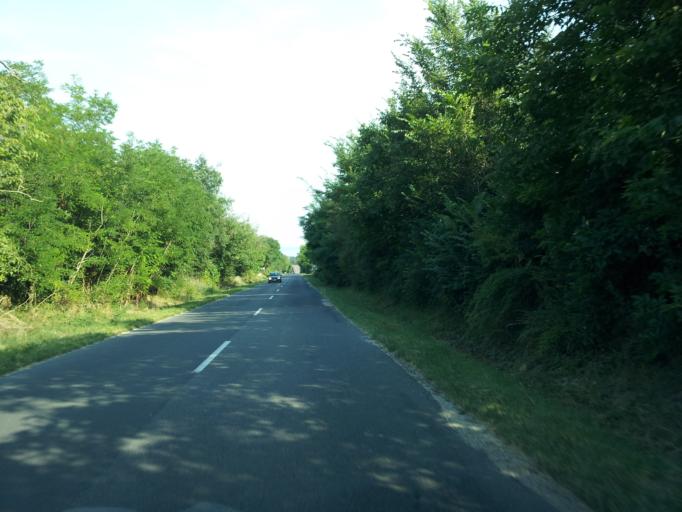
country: HU
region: Veszprem
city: Balatonkenese
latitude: 47.0474
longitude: 18.0927
